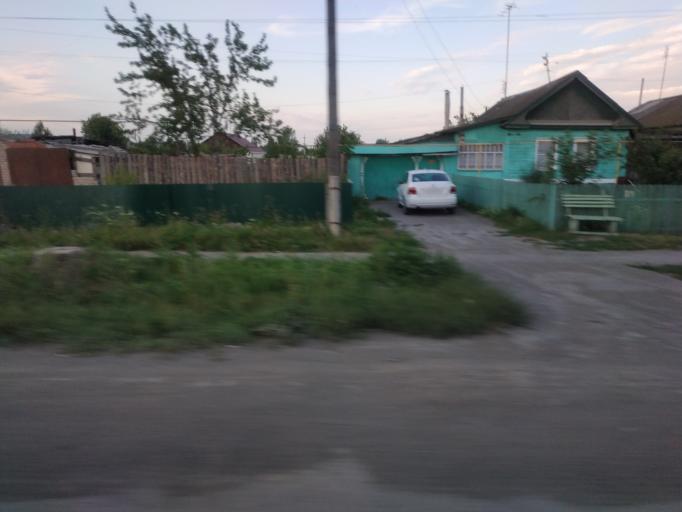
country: RU
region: Sverdlovsk
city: Bogdanovich
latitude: 56.7631
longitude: 62.0695
